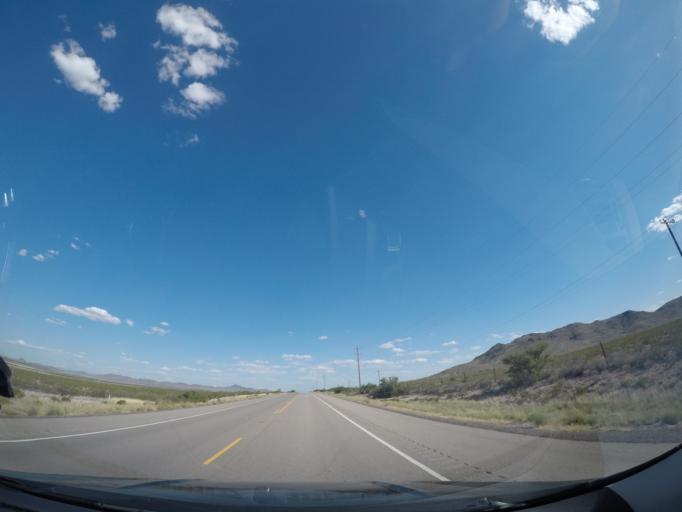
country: US
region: Texas
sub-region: Culberson County
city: Van Horn
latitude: 30.9084
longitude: -104.8019
